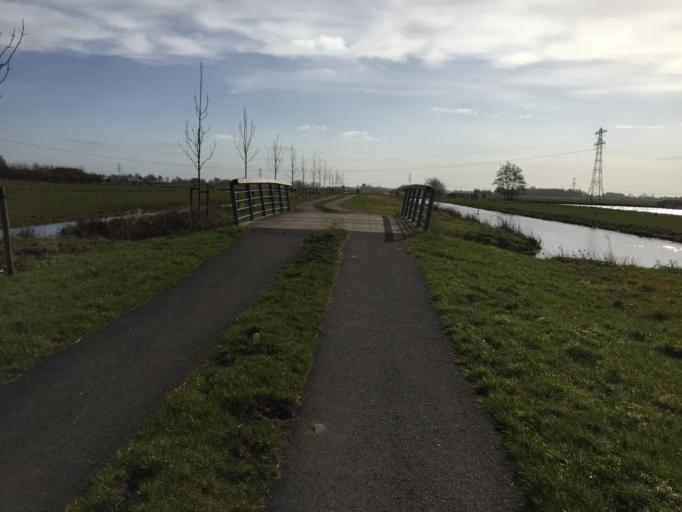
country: NL
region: South Holland
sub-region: Gemeente Gouda
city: Gouda
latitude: 52.0007
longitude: 4.7205
